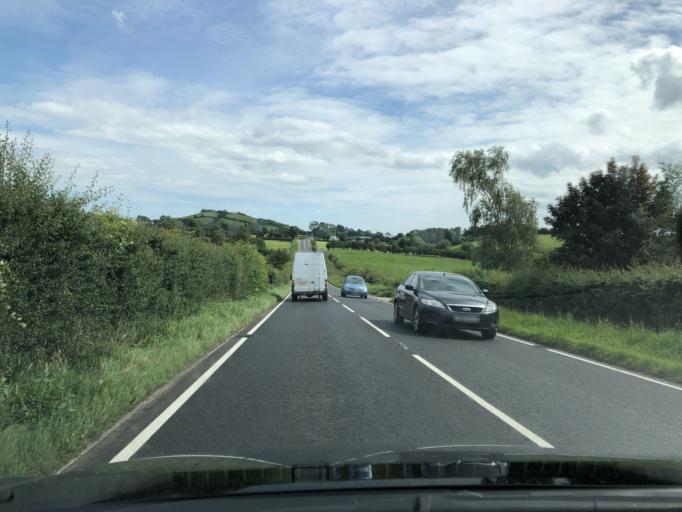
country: GB
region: Northern Ireland
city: Annahilt
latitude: 54.4425
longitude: -5.9441
